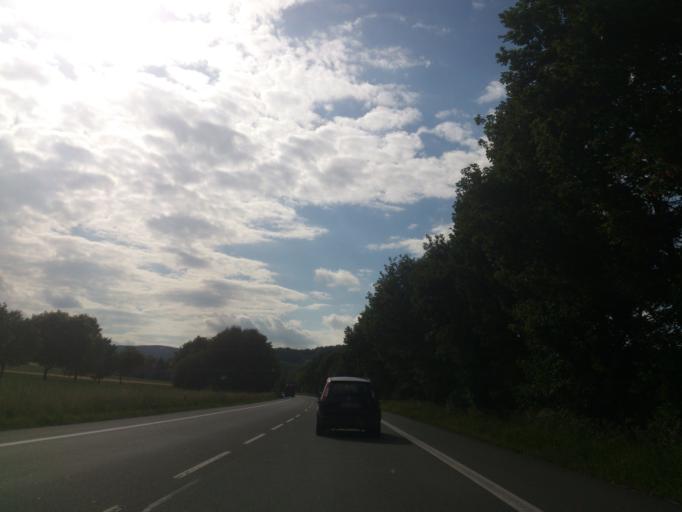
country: DE
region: North Rhine-Westphalia
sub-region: Regierungsbezirk Detmold
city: Bad Driburg
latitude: 51.7223
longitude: 9.0590
